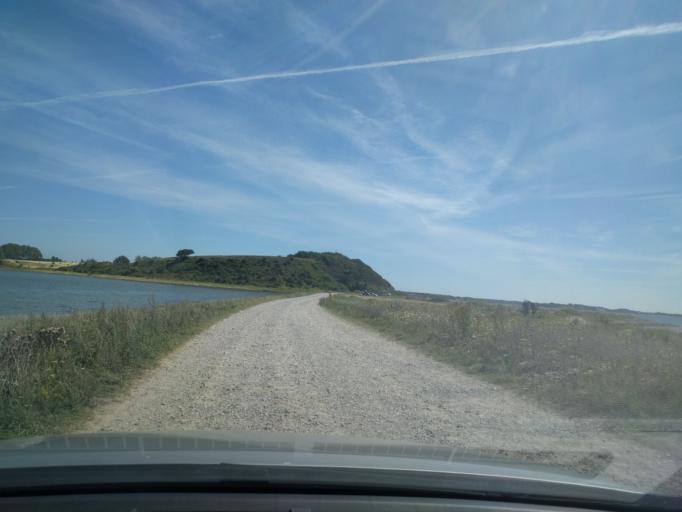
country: DK
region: South Denmark
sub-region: Kerteminde Kommune
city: Munkebo
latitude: 55.6102
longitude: 10.5978
